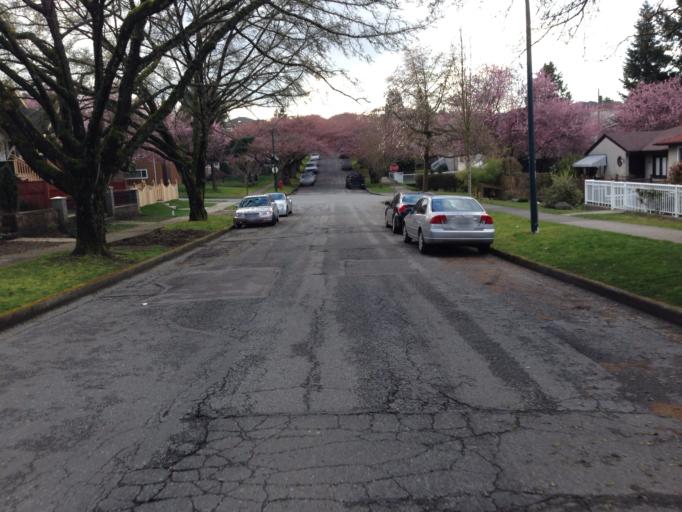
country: CA
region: British Columbia
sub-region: Fraser Valley Regional District
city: North Vancouver
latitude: 49.2704
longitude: -123.0356
